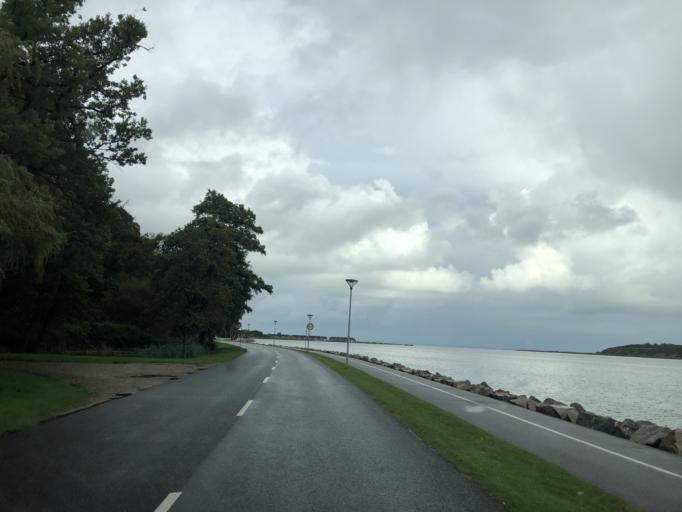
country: DK
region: Central Jutland
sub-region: Lemvig Kommune
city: Lemvig
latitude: 56.5552
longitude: 8.2959
